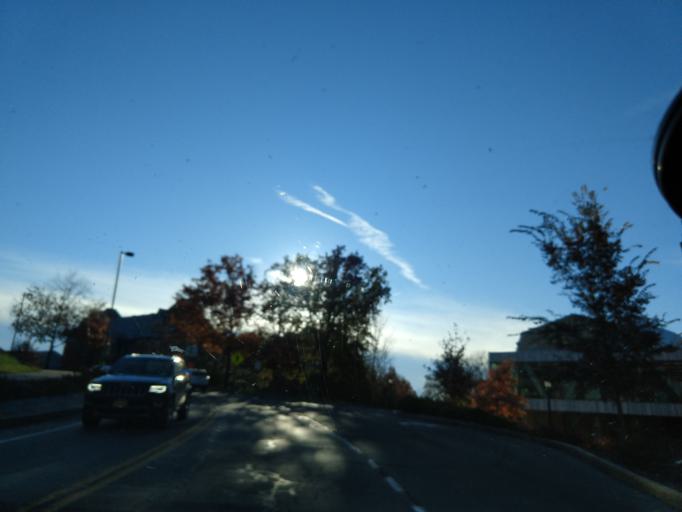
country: US
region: New York
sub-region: Tompkins County
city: Cayuga Heights
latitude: 42.4511
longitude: -76.4825
